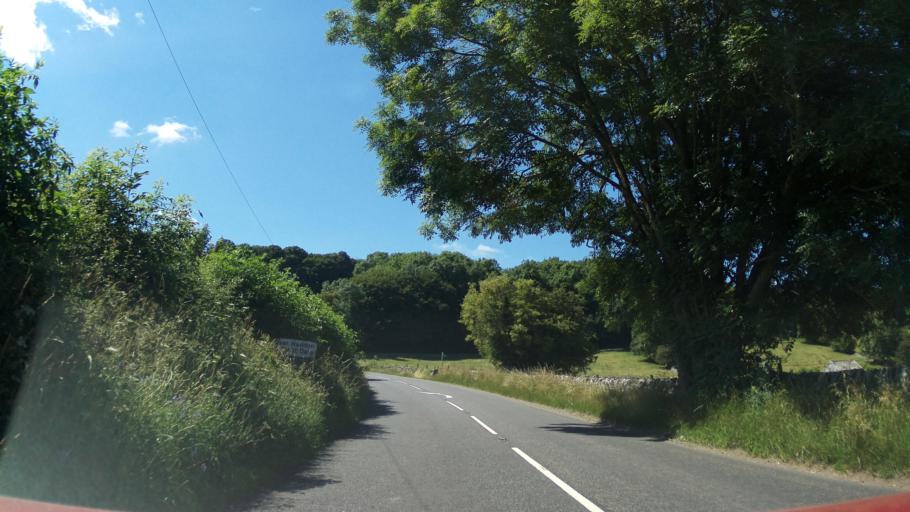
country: GB
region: England
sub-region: Derbyshire
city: Bakewell
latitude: 53.2075
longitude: -1.6916
